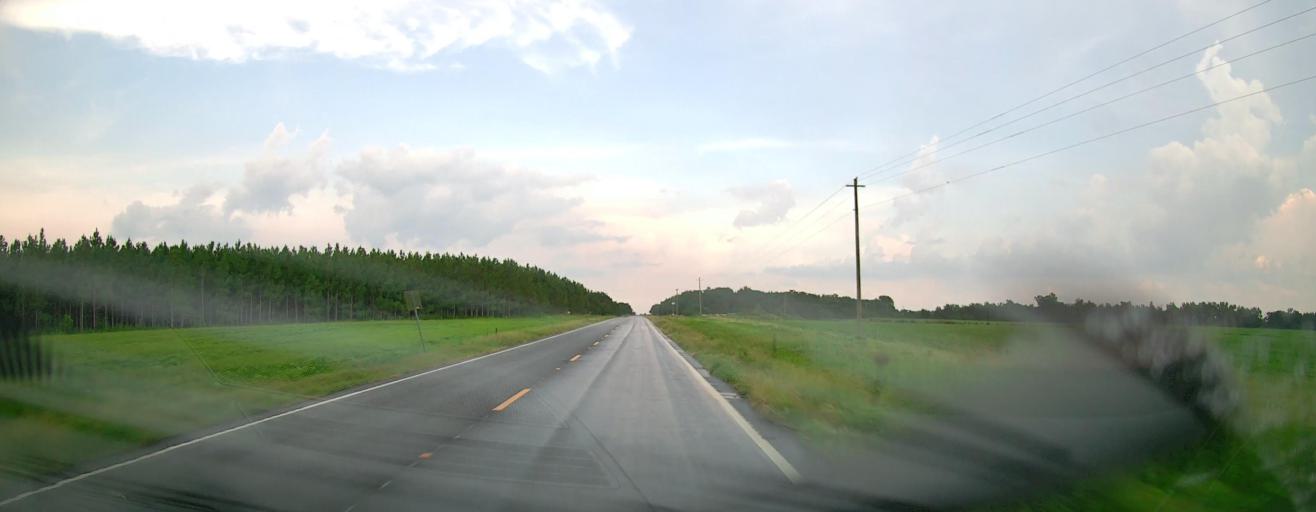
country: US
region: Georgia
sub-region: Dodge County
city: Chester
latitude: 32.5514
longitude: -83.1348
